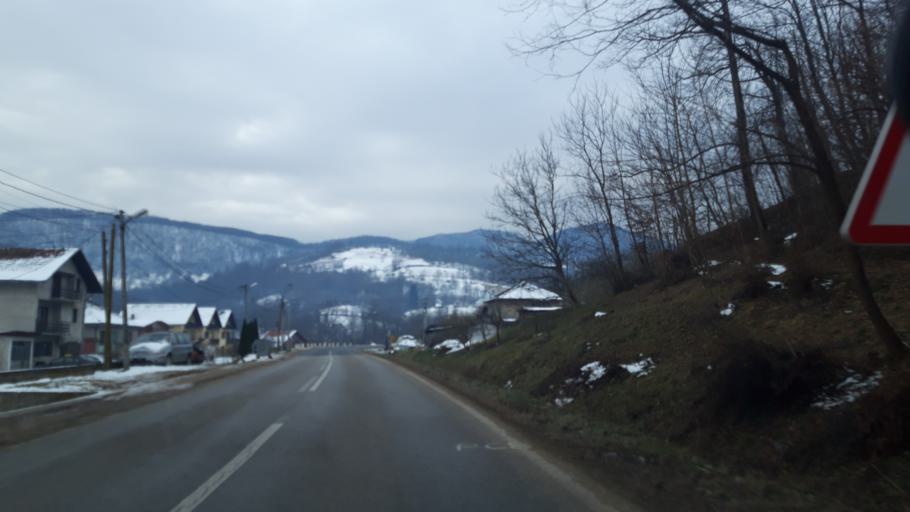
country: BA
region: Republika Srpska
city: Milici
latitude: 44.1651
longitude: 19.0678
